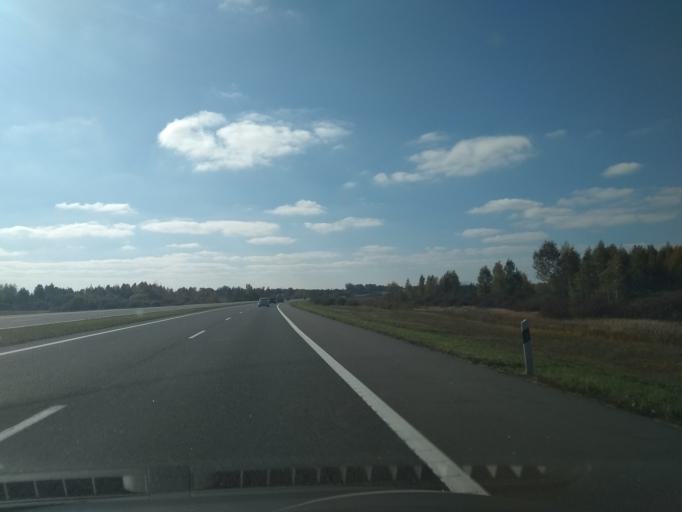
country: BY
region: Brest
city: Baranovichi
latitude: 53.1510
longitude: 25.9704
